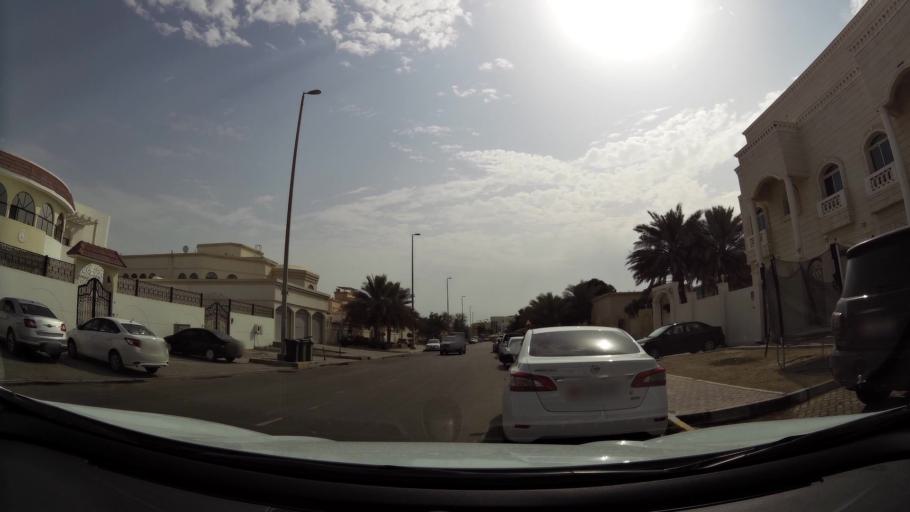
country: AE
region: Abu Dhabi
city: Abu Dhabi
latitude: 24.4432
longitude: 54.4195
